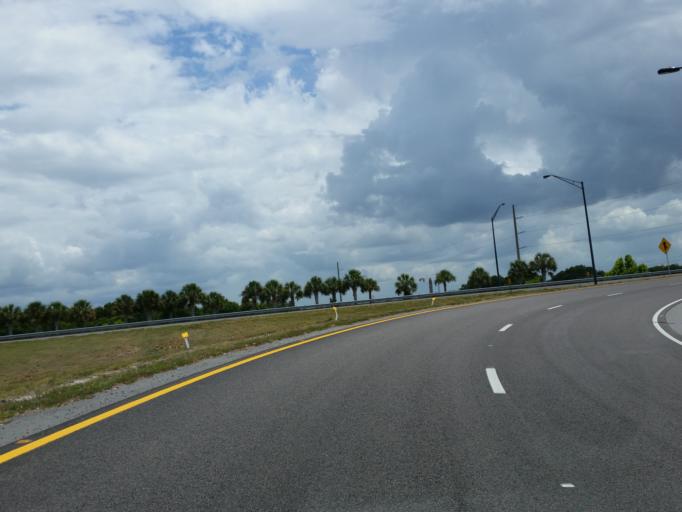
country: US
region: Florida
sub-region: Polk County
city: Crystal Lake
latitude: 28.0019
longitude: -81.9007
